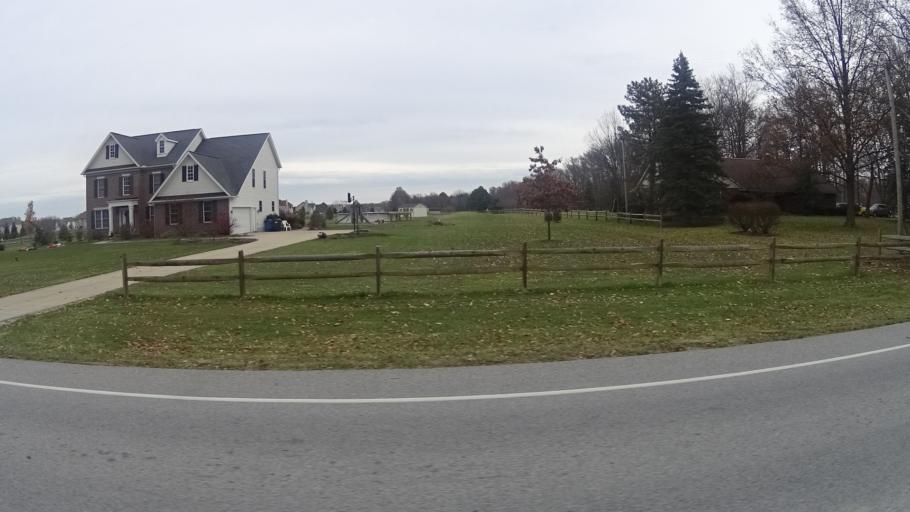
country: US
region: Ohio
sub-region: Cuyahoga County
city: Olmsted Falls
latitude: 41.3443
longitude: -81.9428
